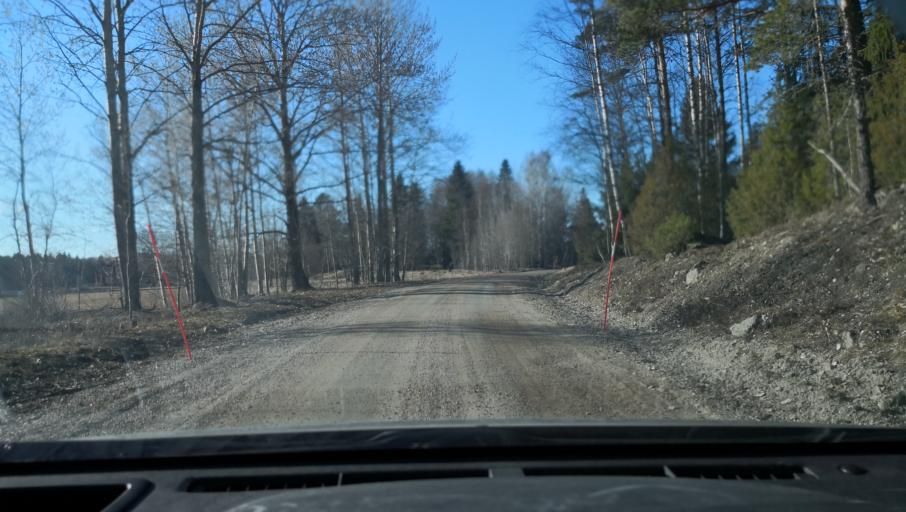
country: SE
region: Vaestmanland
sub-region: Sala Kommun
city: Sala
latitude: 60.1461
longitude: 16.6430
